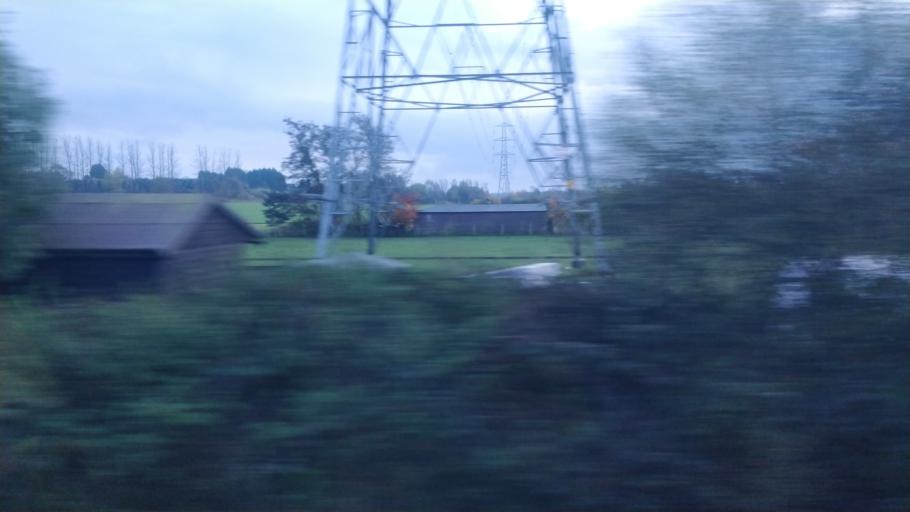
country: GB
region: England
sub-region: Lancashire
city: Parbold
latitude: 53.5962
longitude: -2.7970
